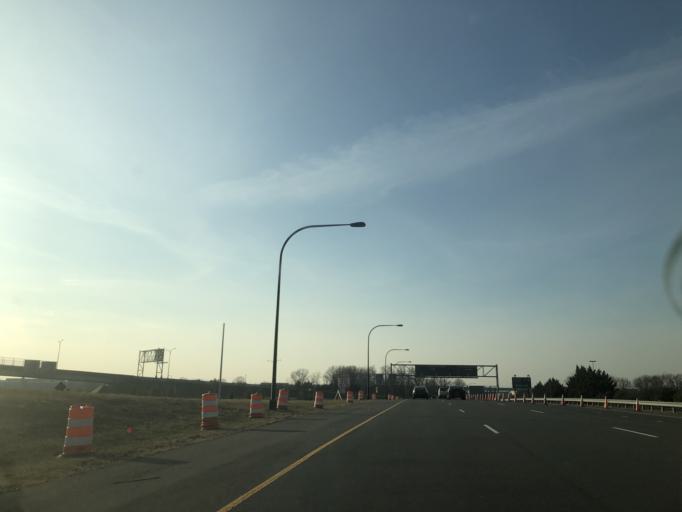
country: US
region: Virginia
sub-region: Fairfax County
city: Floris
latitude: 38.9630
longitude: -77.4398
